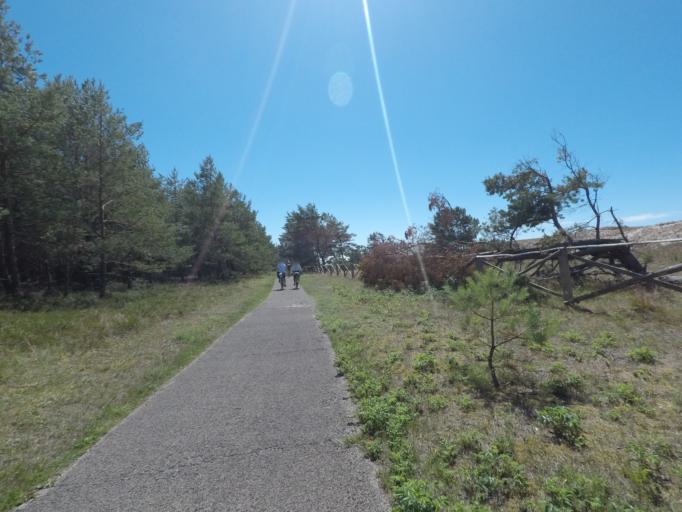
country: LT
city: Neringa
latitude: 55.4887
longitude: 21.0850
